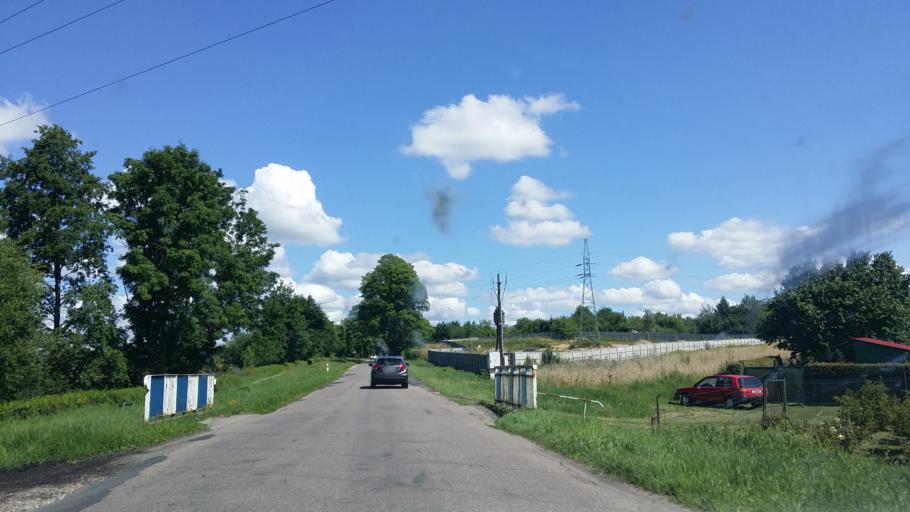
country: PL
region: West Pomeranian Voivodeship
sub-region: Powiat swidwinski
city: Swidwin
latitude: 53.7563
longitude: 15.7641
